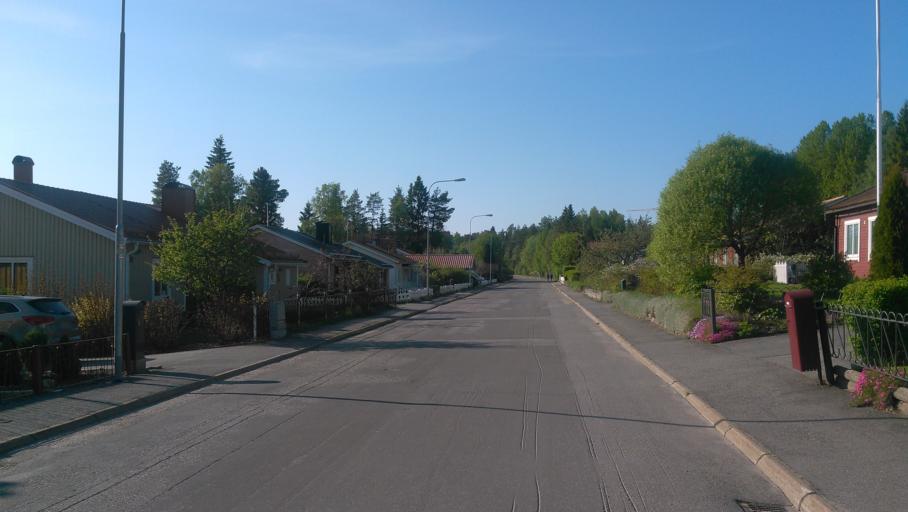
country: SE
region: Vaesterbotten
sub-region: Umea Kommun
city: Umea
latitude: 63.8083
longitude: 20.3060
